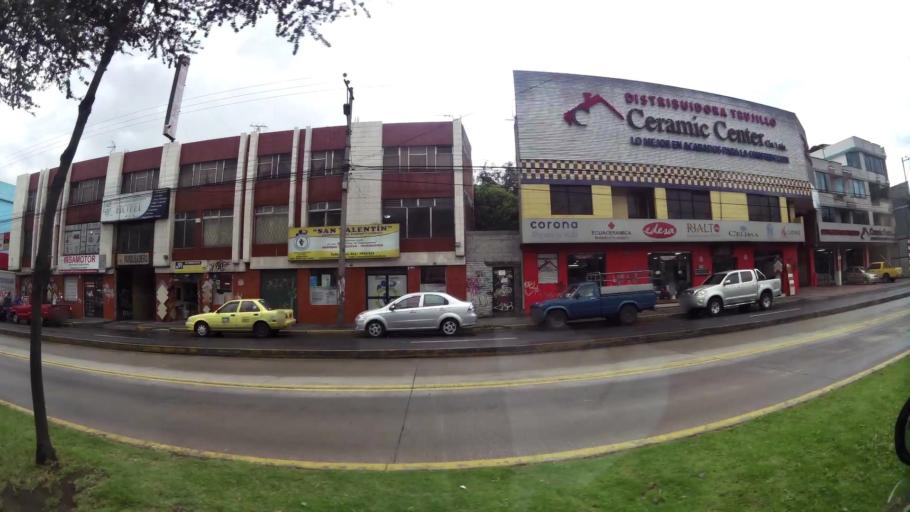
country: EC
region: Pichincha
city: Quito
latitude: -0.2682
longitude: -78.5515
